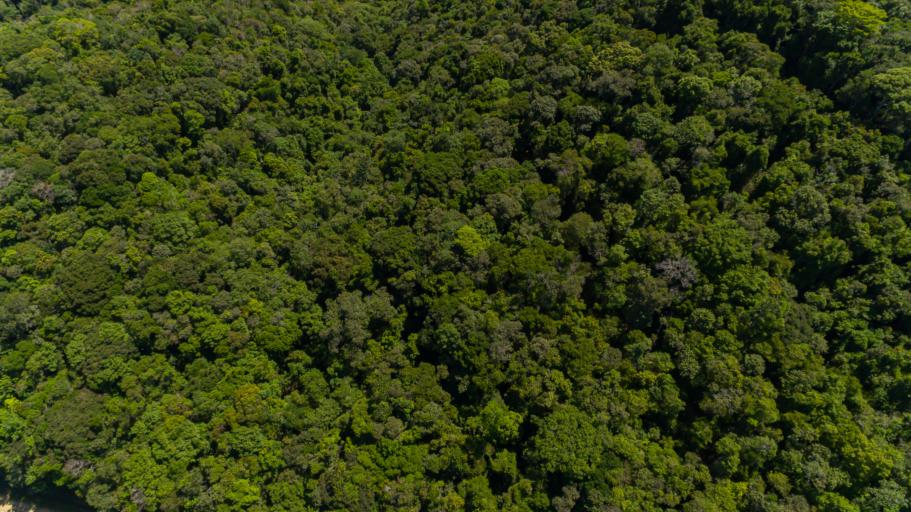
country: BR
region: Sao Paulo
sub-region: Juquitiba
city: Juquitiba
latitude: -24.0247
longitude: -47.2448
